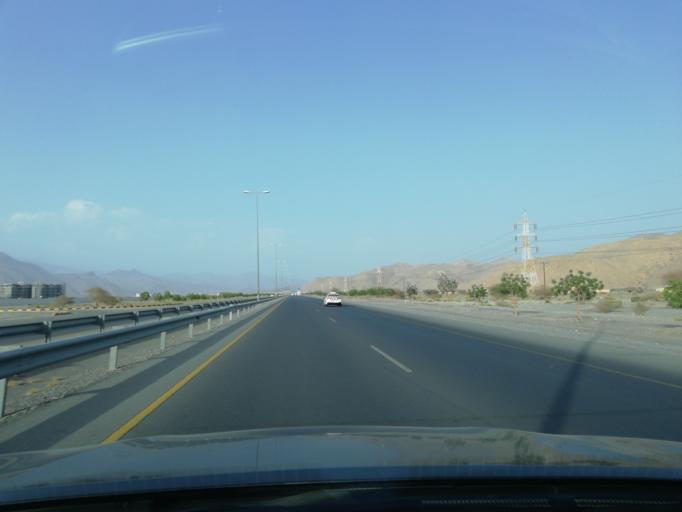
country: OM
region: Muhafazat ad Dakhiliyah
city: Nizwa
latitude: 22.8662
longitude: 57.6005
